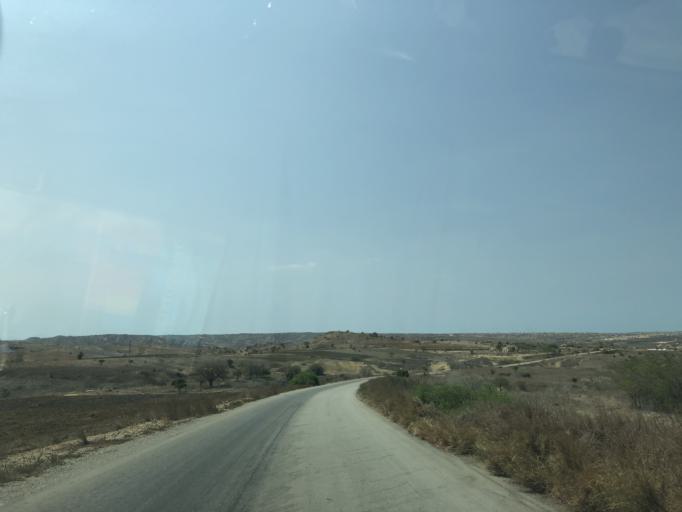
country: AO
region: Cuanza Sul
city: Sumbe
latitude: -10.6703
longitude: 13.7873
